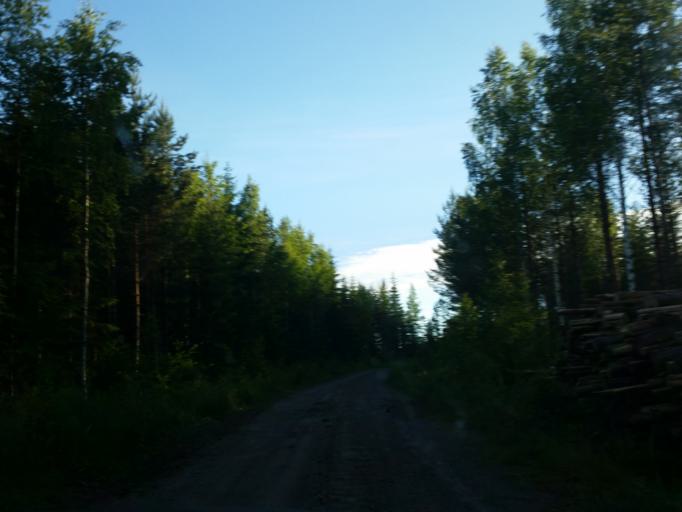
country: FI
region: Northern Savo
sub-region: Sisae-Savo
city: Tervo
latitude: 63.0568
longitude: 26.6329
